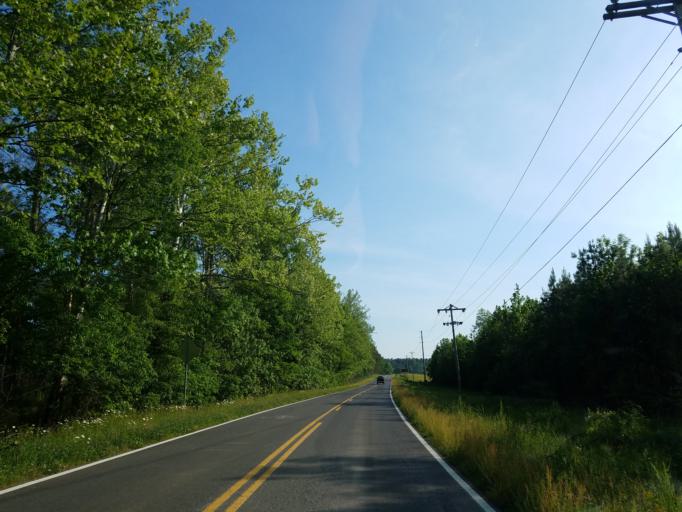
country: US
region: Georgia
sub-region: Chattooga County
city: Trion
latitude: 34.5871
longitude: -85.1425
